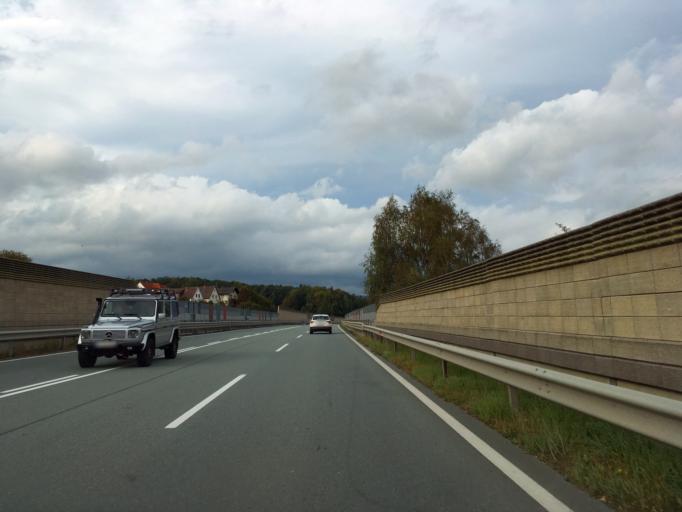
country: AT
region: Styria
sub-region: Politischer Bezirk Hartberg-Fuerstenfeld
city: Rohrbach an der Lafnitz
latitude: 47.3979
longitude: 16.0019
